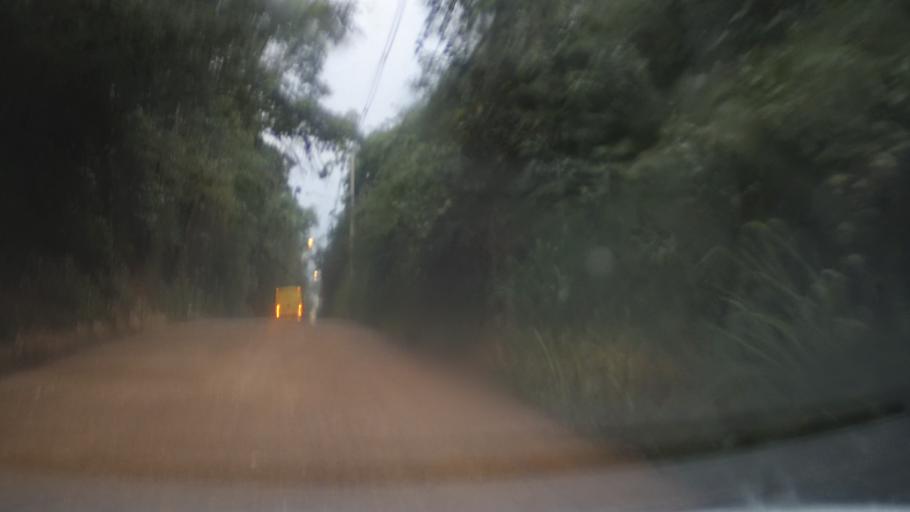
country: BR
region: Sao Paulo
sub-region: Itupeva
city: Itupeva
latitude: -23.1938
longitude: -46.9894
